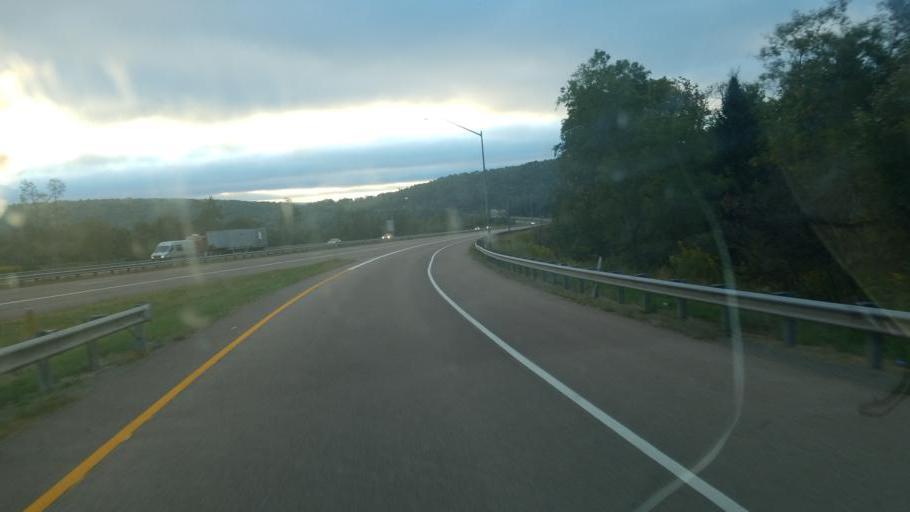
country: US
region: Pennsylvania
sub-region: Somerset County
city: Meyersdale
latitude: 39.6863
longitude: -79.2454
